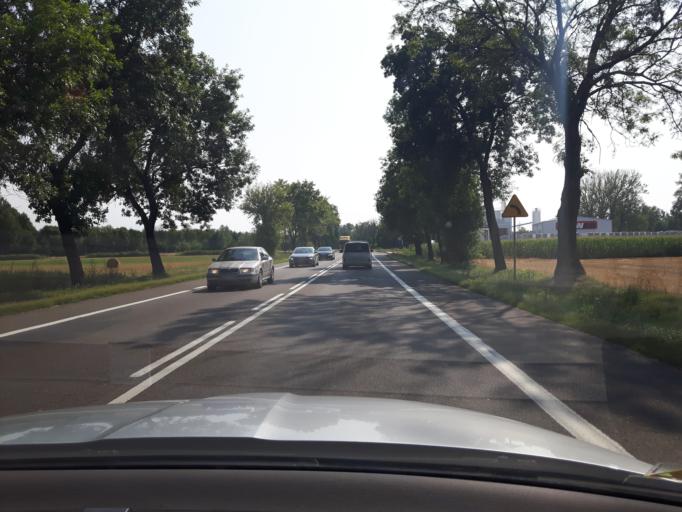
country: PL
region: Masovian Voivodeship
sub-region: Powiat ciechanowski
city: Glinojeck
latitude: 52.8301
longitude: 20.2615
